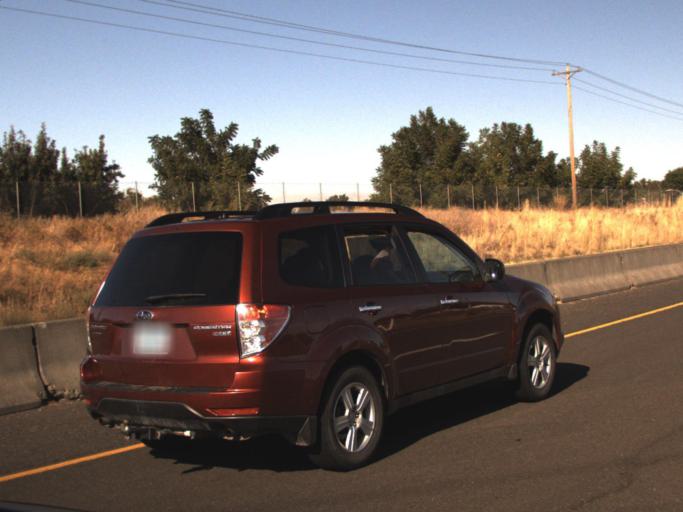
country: US
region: Washington
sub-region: Walla Walla County
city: College Place
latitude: 46.0349
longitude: -118.3747
